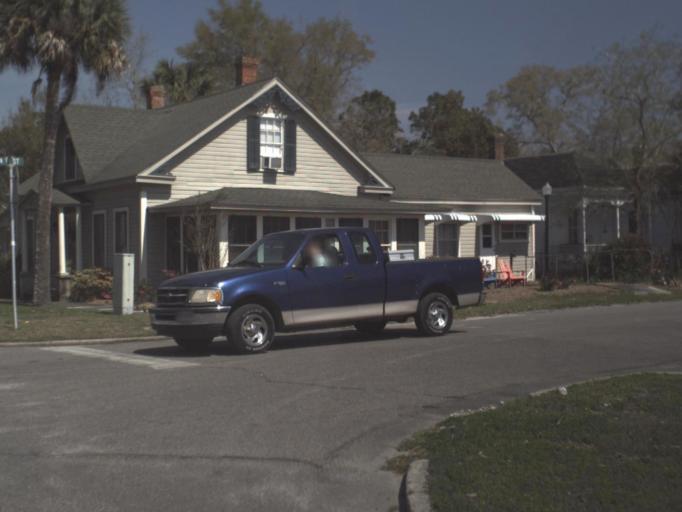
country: US
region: Florida
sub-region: Franklin County
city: Apalachicola
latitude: 29.7231
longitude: -84.9893
